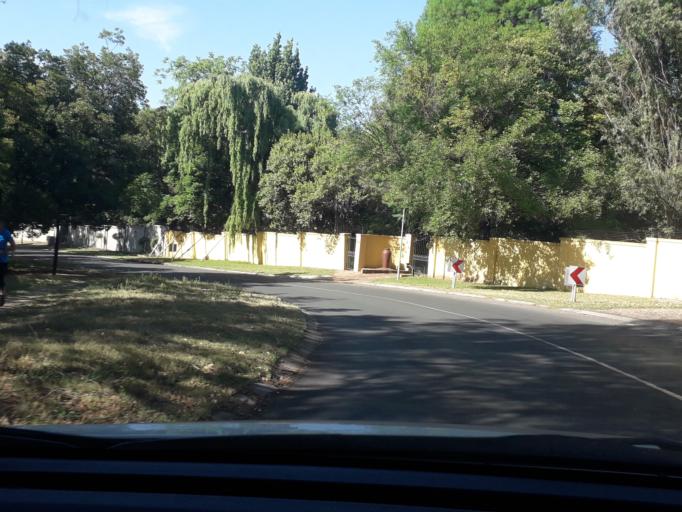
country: ZA
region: Gauteng
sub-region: City of Johannesburg Metropolitan Municipality
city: Midrand
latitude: -26.0686
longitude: 28.0333
